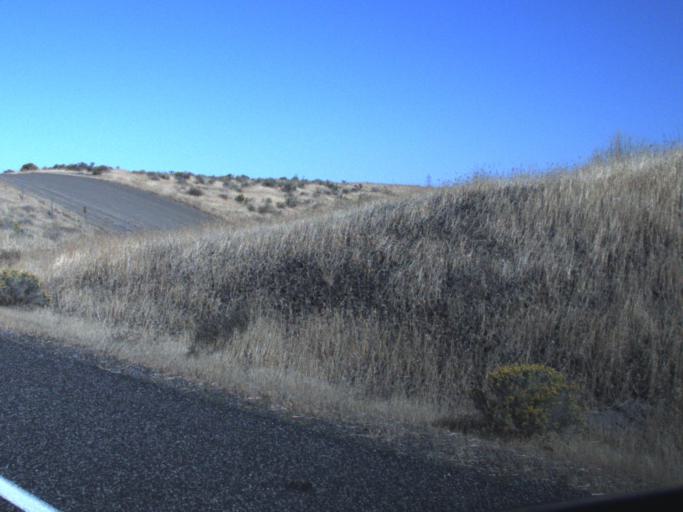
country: US
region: Washington
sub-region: Benton County
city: West Richland
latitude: 46.3850
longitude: -119.4260
